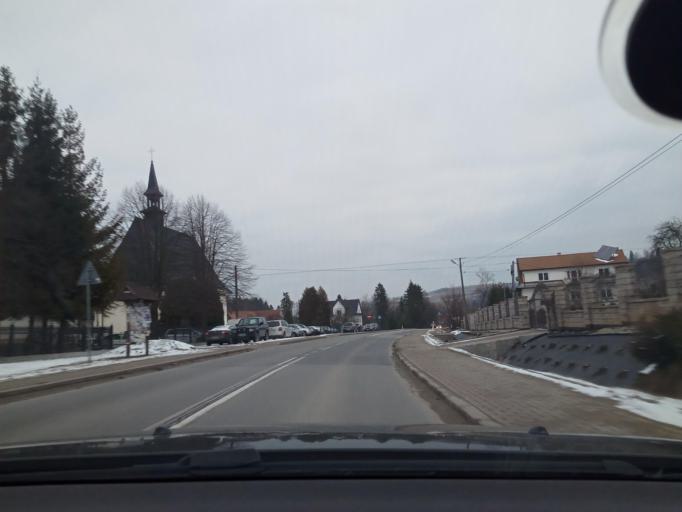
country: PL
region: Lesser Poland Voivodeship
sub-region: Powiat limanowski
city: Mszana Gorna
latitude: 49.6302
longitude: 20.1413
